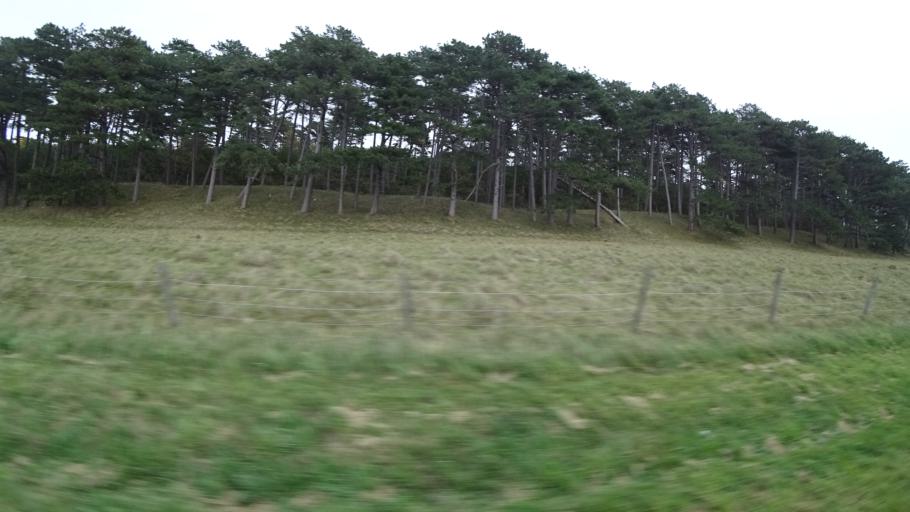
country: SE
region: Skane
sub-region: Kavlinge Kommun
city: Hofterup
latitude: 55.8099
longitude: 12.9368
